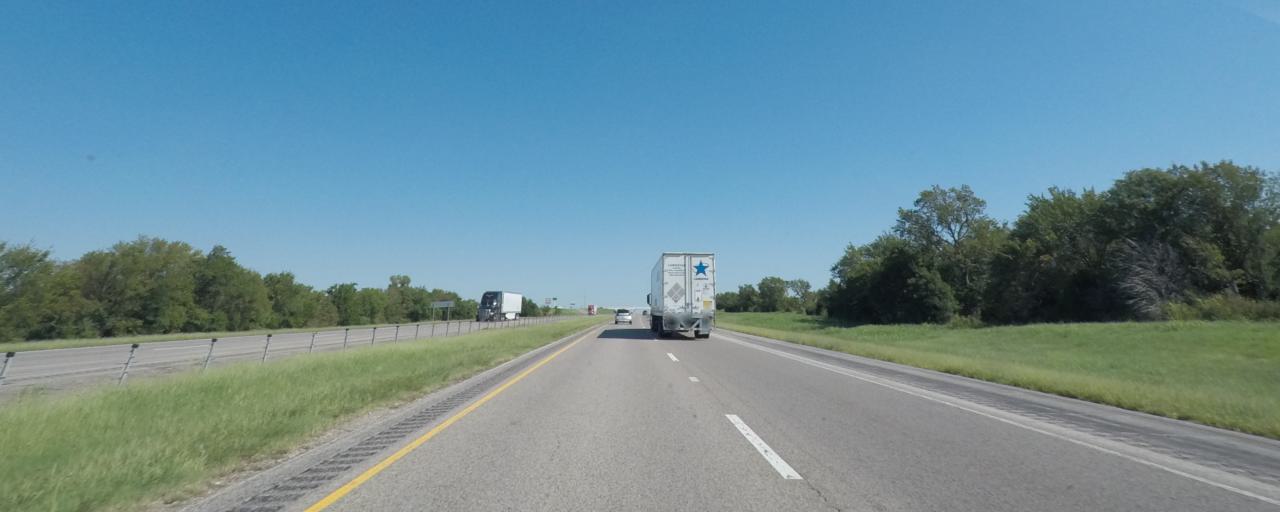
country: US
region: Oklahoma
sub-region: Noble County
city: Perry
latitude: 36.2684
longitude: -97.3276
